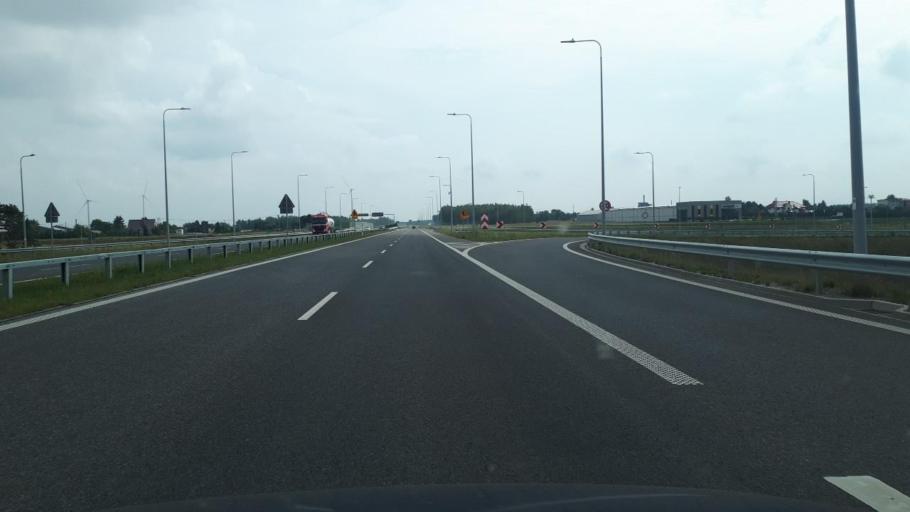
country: PL
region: Greater Poland Voivodeship
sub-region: Powiat kepinski
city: Baranow
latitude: 51.2927
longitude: 18.0210
